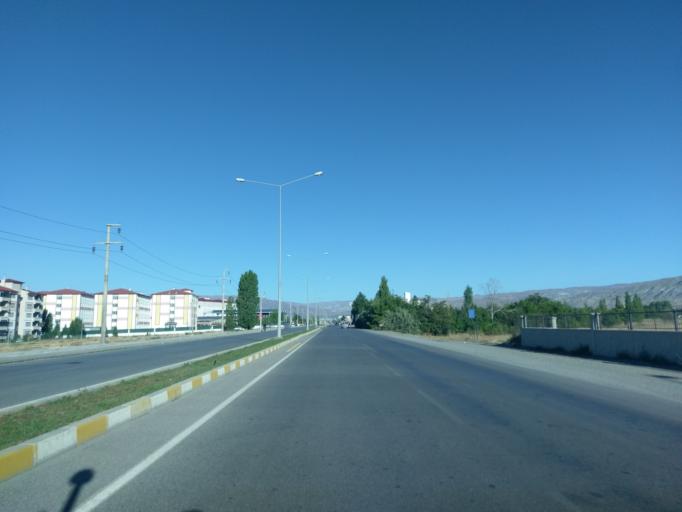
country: TR
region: Erzincan
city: Erzincan
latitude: 39.7579
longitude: 39.4464
